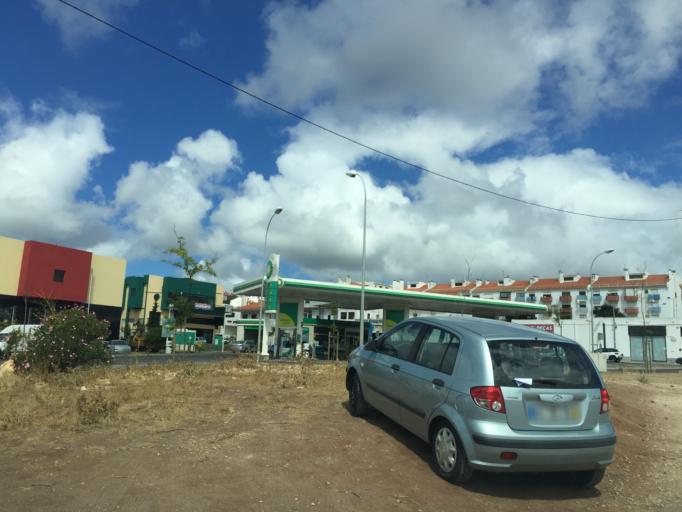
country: PT
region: Lisbon
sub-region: Odivelas
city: Famoes
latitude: 38.7766
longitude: -9.2295
